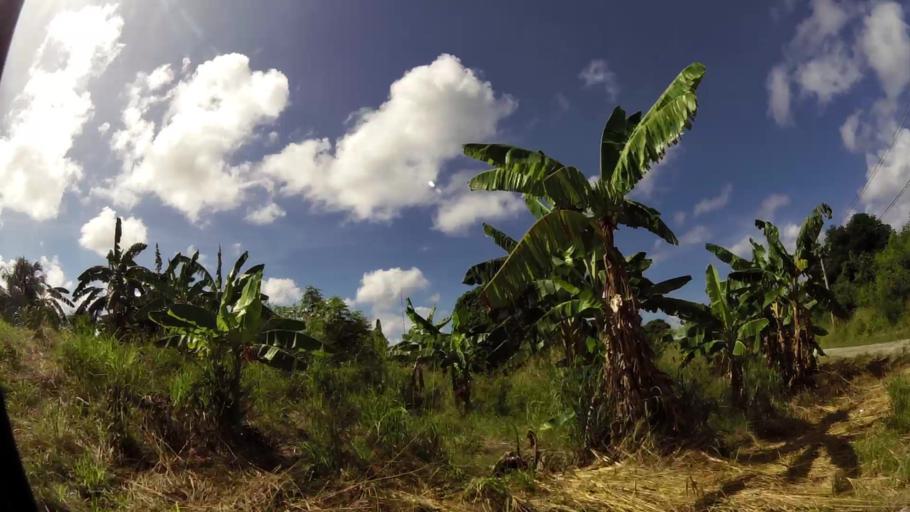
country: BB
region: Saint Peter
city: Speightstown
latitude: 13.2602
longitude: -59.6336
